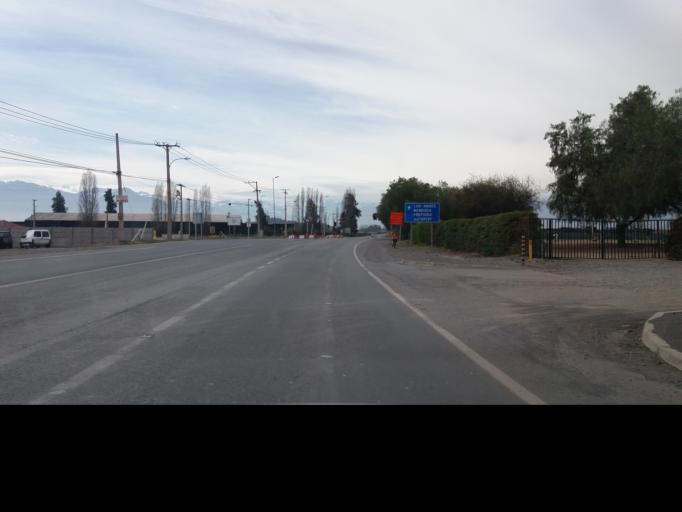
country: CL
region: Valparaiso
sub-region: Provincia de San Felipe
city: San Felipe
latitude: -32.7739
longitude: -70.7109
